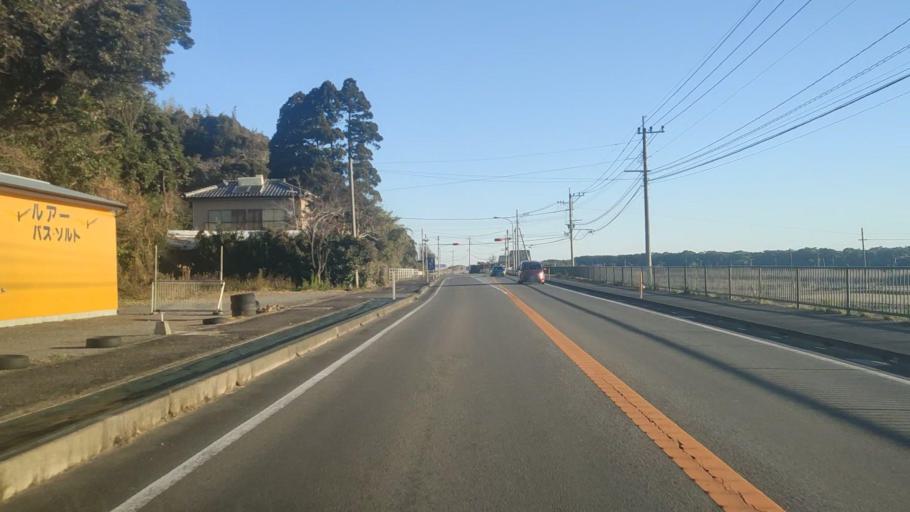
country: JP
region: Miyazaki
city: Takanabe
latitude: 32.0947
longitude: 131.5165
